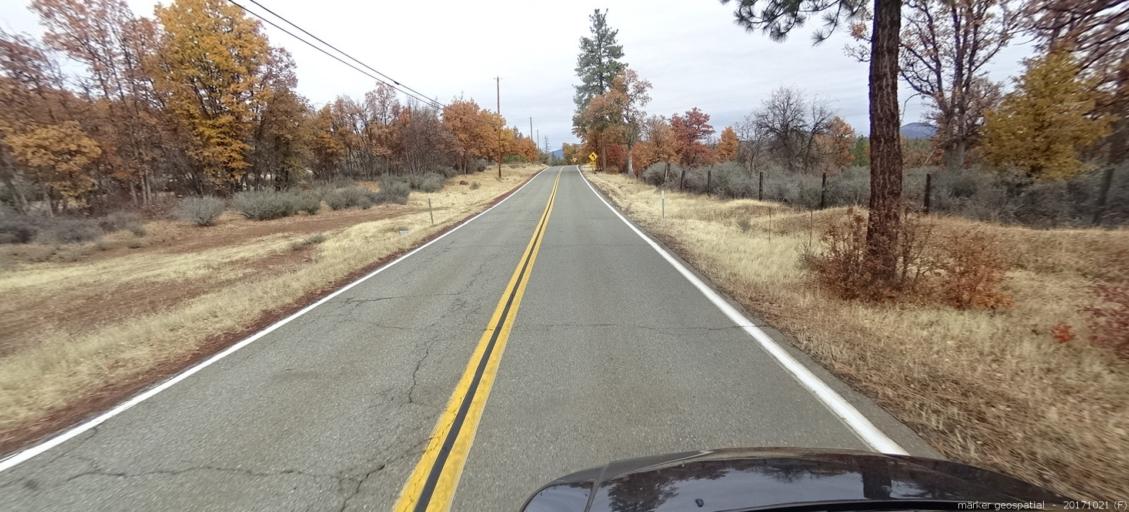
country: US
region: California
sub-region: Shasta County
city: Burney
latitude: 40.9299
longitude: -121.5663
